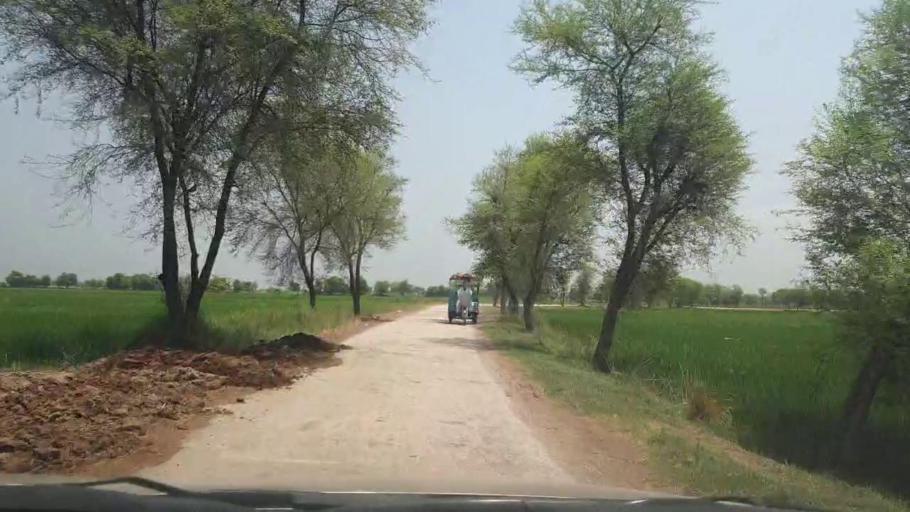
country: PK
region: Sindh
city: Ratodero
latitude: 27.7338
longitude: 68.2941
